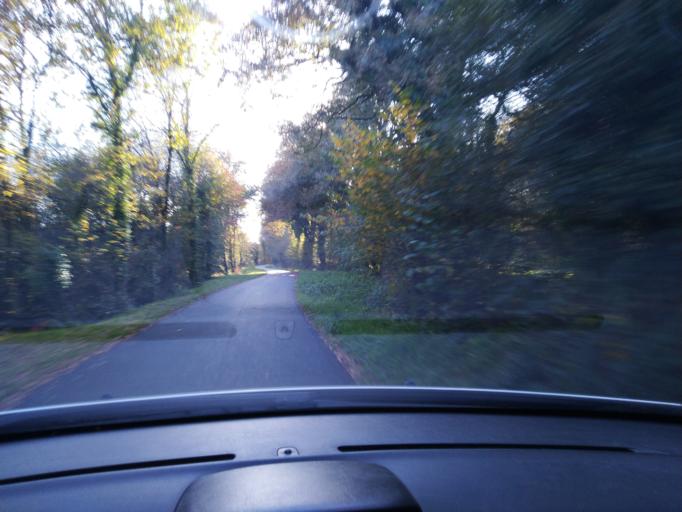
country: FR
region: Brittany
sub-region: Departement du Finistere
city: Guerlesquin
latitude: 48.5109
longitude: -3.5786
